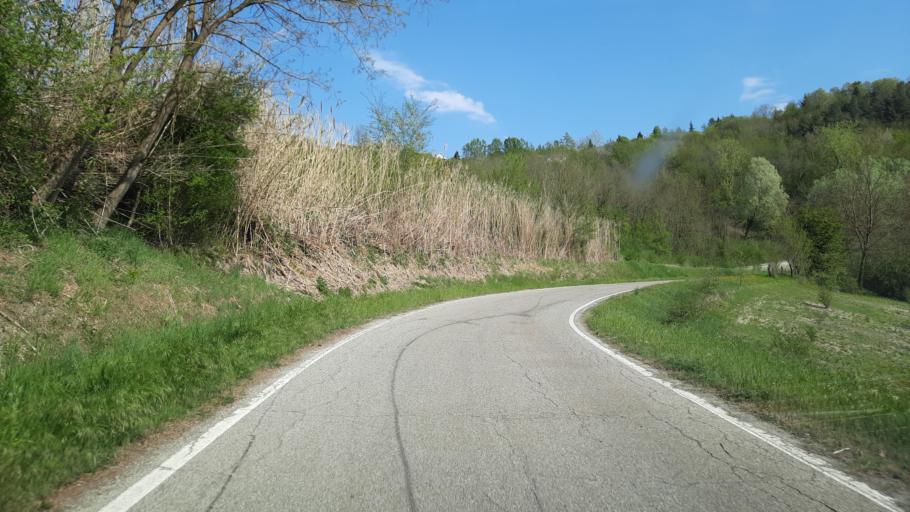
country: IT
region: Piedmont
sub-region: Provincia di Alessandria
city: Villamiroglio
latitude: 45.1380
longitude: 8.1675
